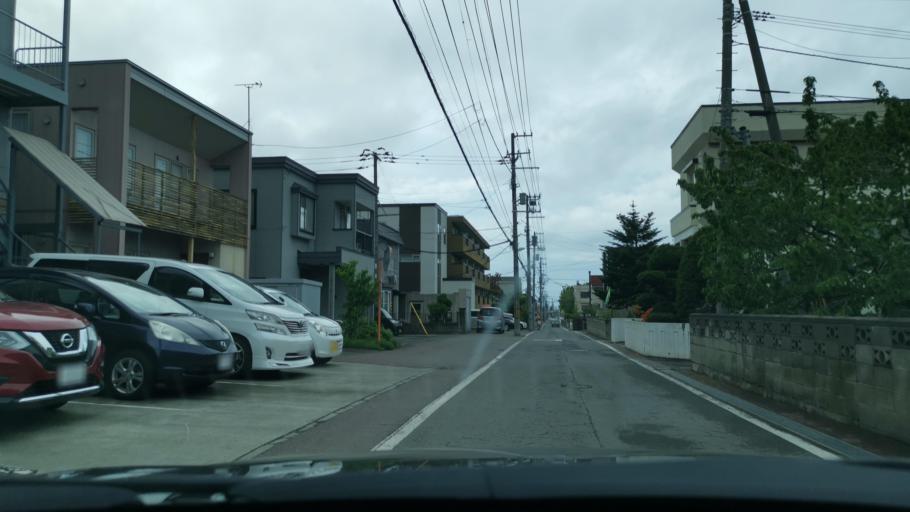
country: JP
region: Hokkaido
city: Sapporo
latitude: 43.0826
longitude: 141.2967
